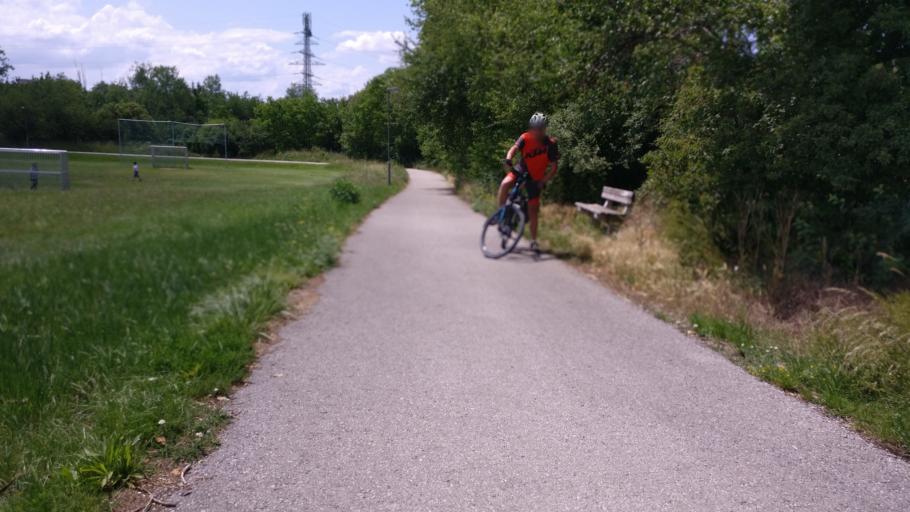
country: AT
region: Lower Austria
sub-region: Politischer Bezirk Wiener Neustadt
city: Lichtenworth
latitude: 47.8311
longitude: 16.2602
